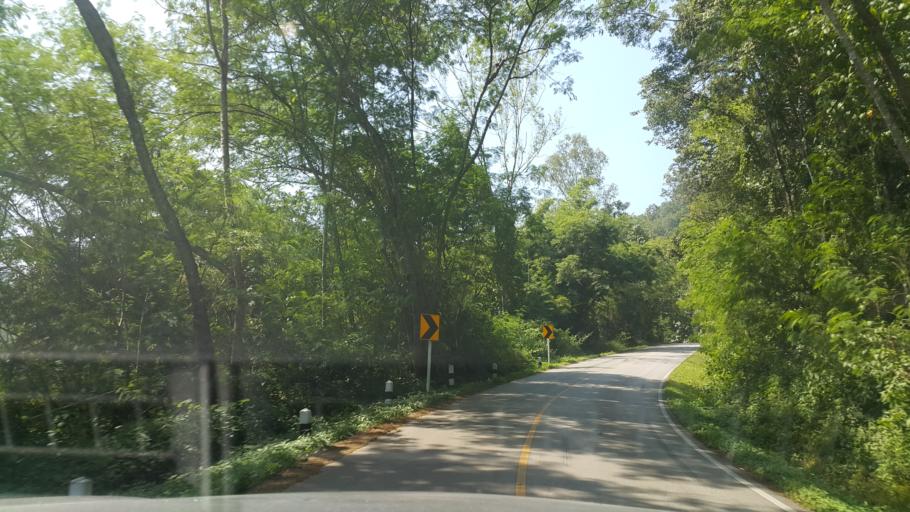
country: TH
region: Chiang Mai
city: Samoeng
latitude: 18.8557
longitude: 98.6889
